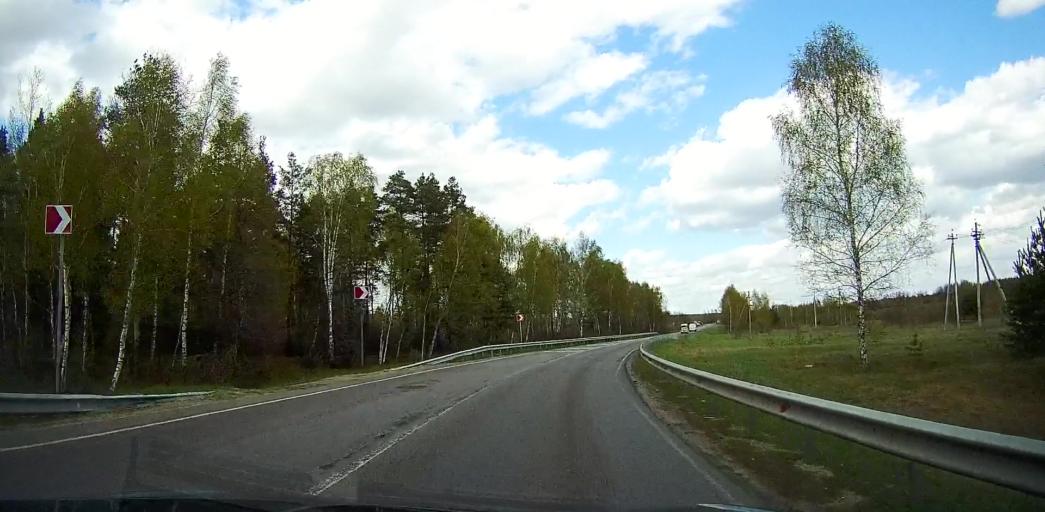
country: RU
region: Moskovskaya
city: Davydovo
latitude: 55.6292
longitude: 38.8628
